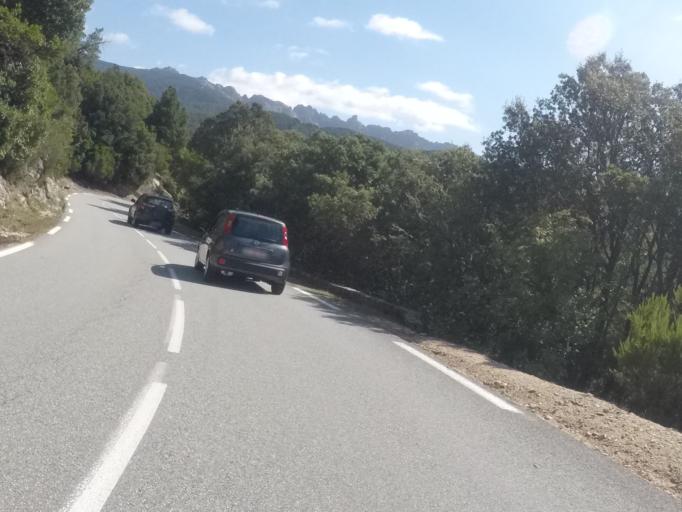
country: FR
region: Corsica
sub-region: Departement de la Corse-du-Sud
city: Zonza
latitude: 41.7672
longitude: 9.1695
